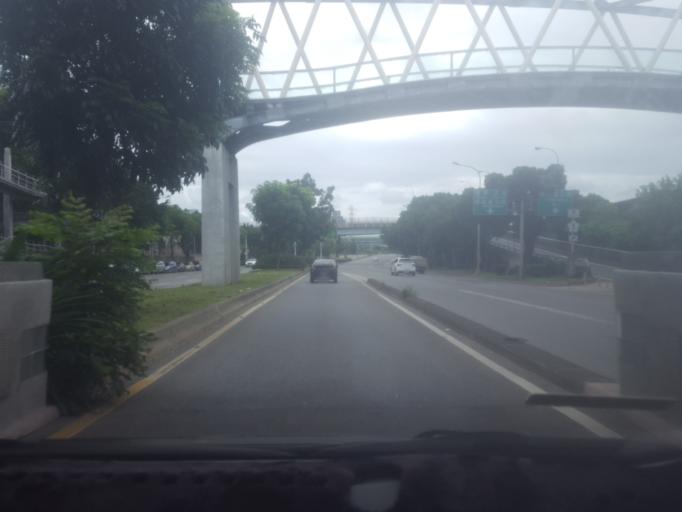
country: TW
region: Taipei
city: Taipei
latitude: 25.0839
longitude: 121.5066
